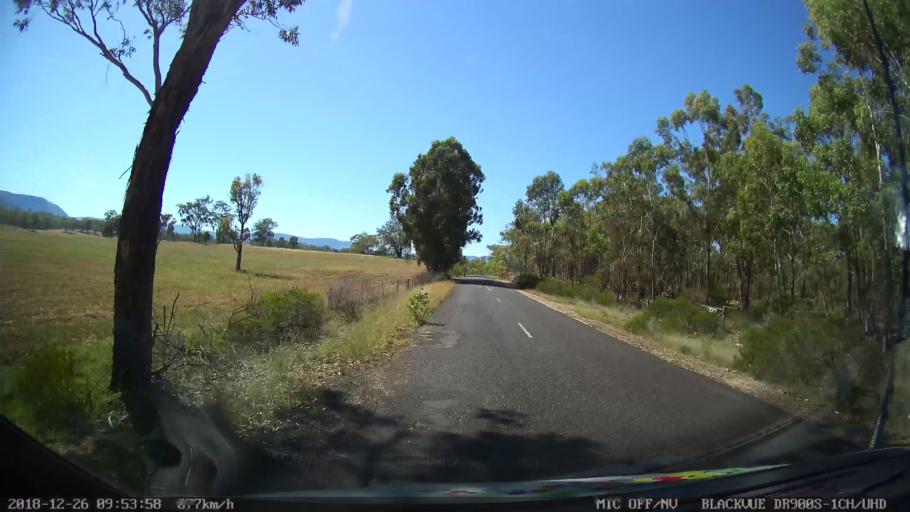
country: AU
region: New South Wales
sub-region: Mid-Western Regional
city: Kandos
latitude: -33.0260
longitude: 150.1573
